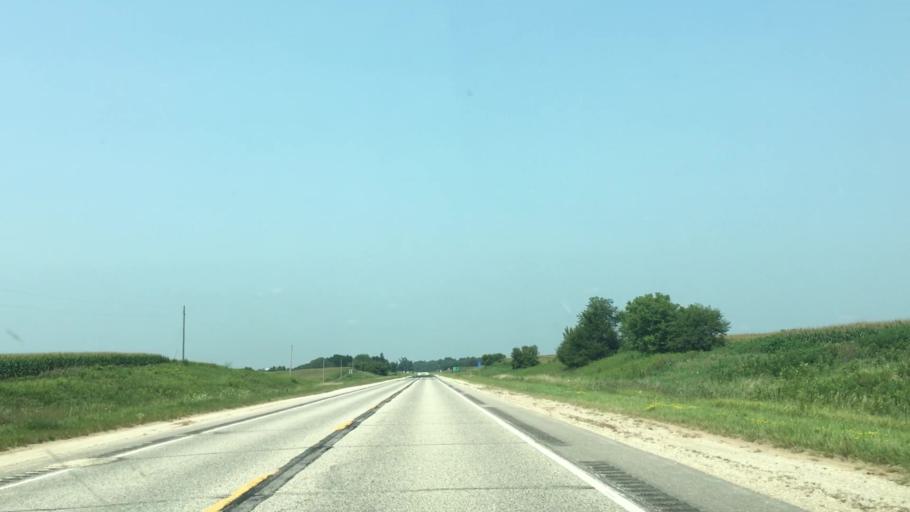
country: US
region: Iowa
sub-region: Fayette County
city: Fayette
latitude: 42.8132
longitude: -91.8051
